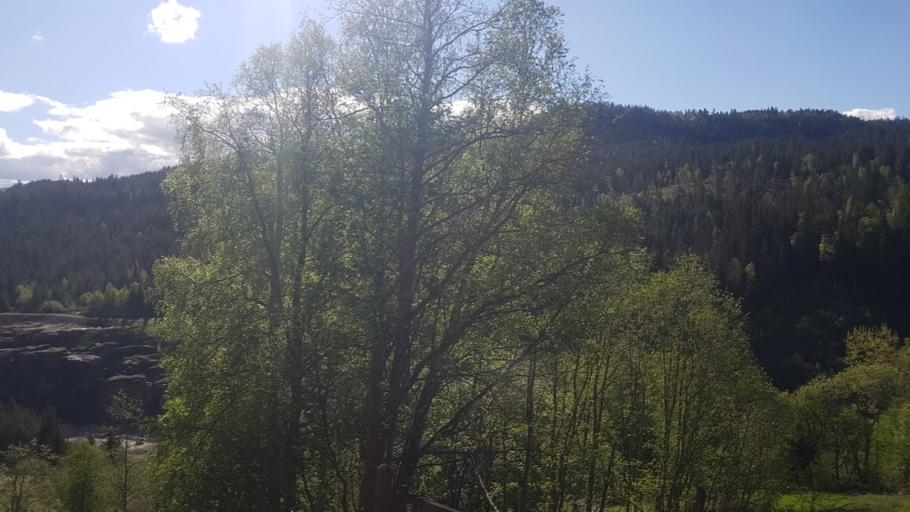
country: NO
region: Sor-Trondelag
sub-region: Midtre Gauldal
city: Storen
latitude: 62.9450
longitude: 10.1897
